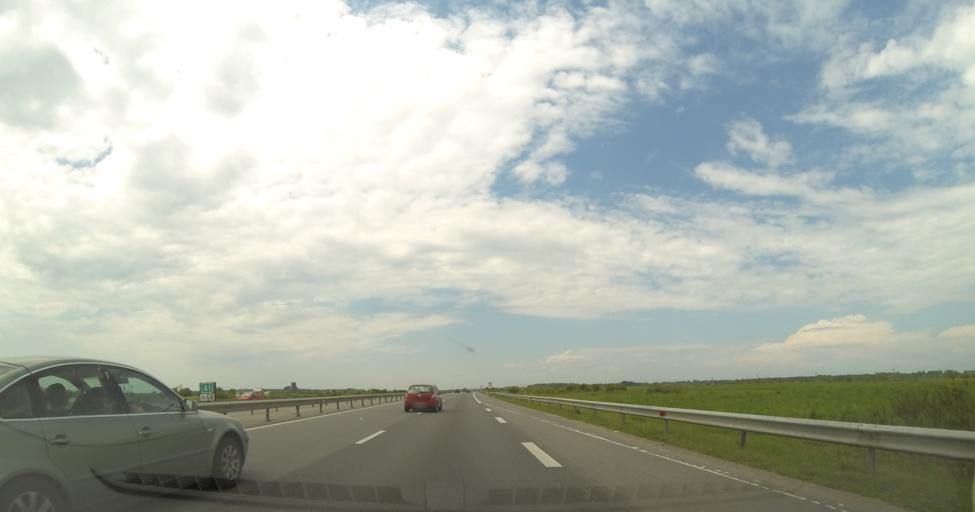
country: RO
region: Dambovita
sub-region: Comuna Mogosani
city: Zavoiu
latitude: 44.6329
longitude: 25.4115
